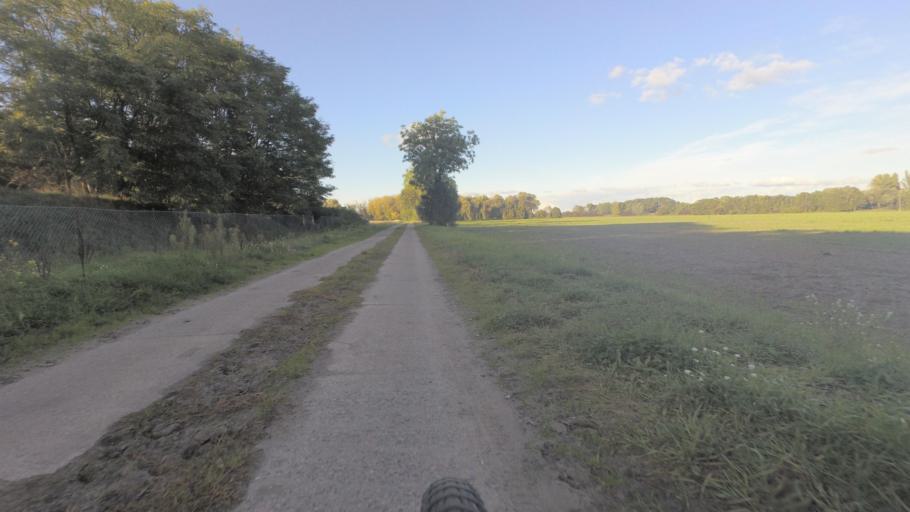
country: DE
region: Brandenburg
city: Rangsdorf
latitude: 52.2810
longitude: 13.3481
